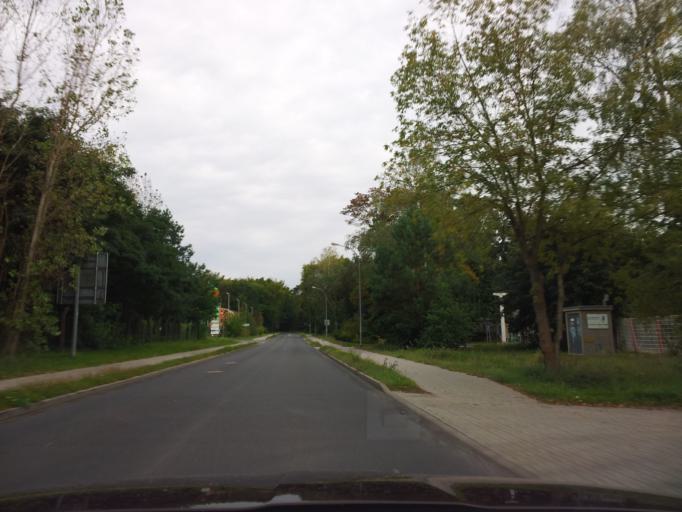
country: DE
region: Brandenburg
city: Ludwigsfelde
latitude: 52.3143
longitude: 13.2636
